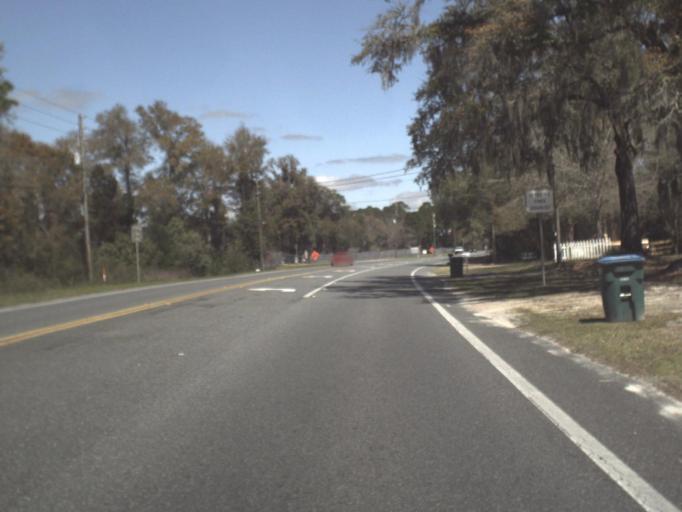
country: US
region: Florida
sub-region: Wakulla County
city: Crawfordville
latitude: 30.0777
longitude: -84.3893
